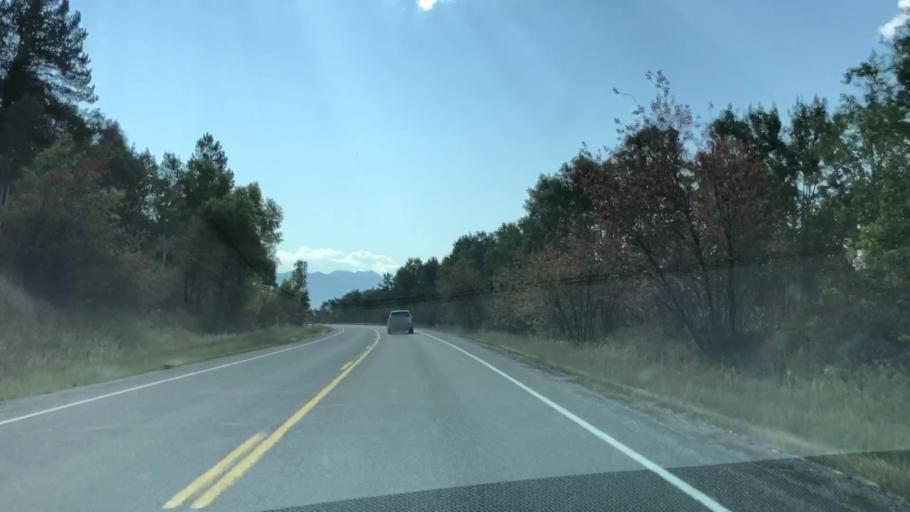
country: US
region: Wyoming
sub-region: Teton County
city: Hoback
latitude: 43.2105
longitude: -111.0587
